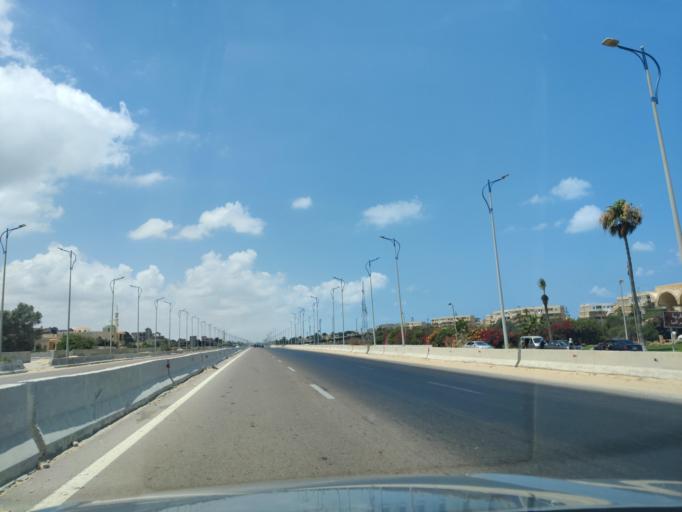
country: EG
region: Muhafazat Matruh
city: Al `Alamayn
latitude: 30.9327
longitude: 29.4823
